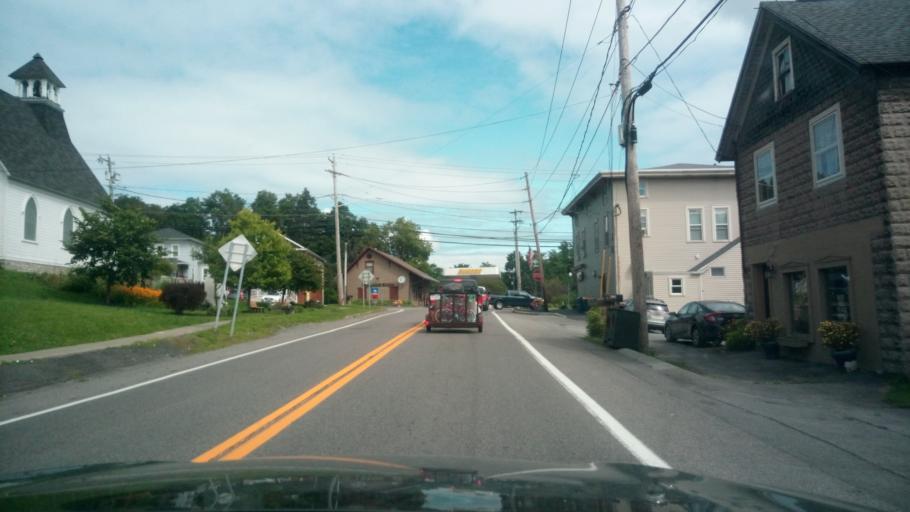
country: US
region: New York
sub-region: Onondaga County
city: Nedrow
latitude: 42.9911
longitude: -76.0715
